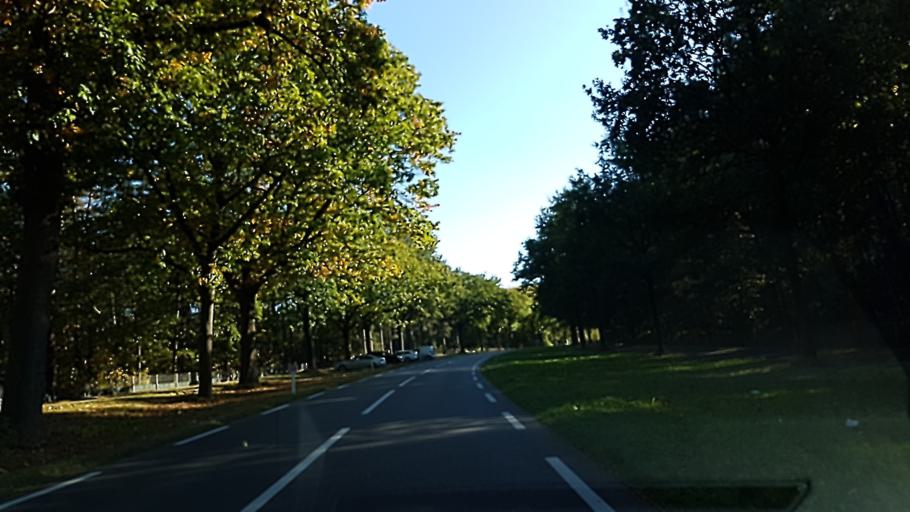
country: BE
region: Flanders
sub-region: Provincie Antwerpen
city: Stabroek
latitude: 51.3793
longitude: 4.3789
